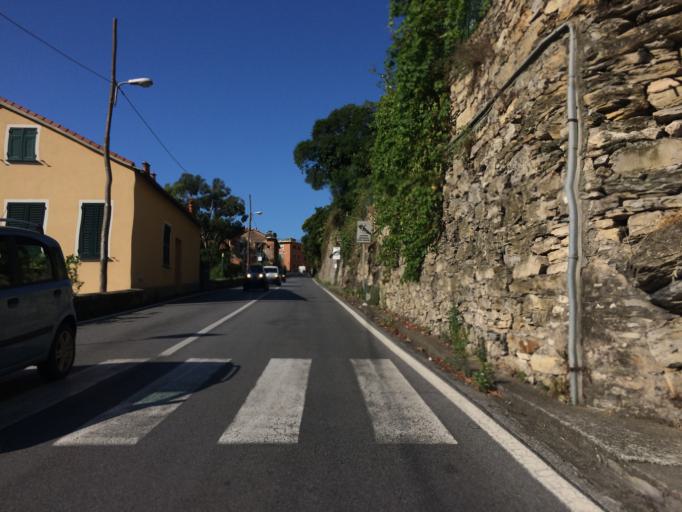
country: IT
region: Liguria
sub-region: Provincia di Genova
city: Zoagli
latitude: 44.3394
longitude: 9.2679
